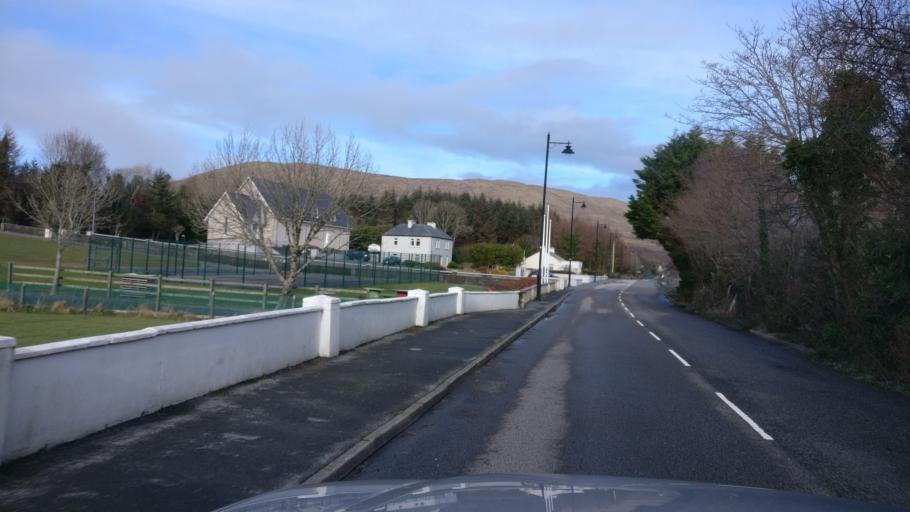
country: IE
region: Connaught
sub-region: County Galway
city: Oughterard
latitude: 53.5113
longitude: -9.4567
